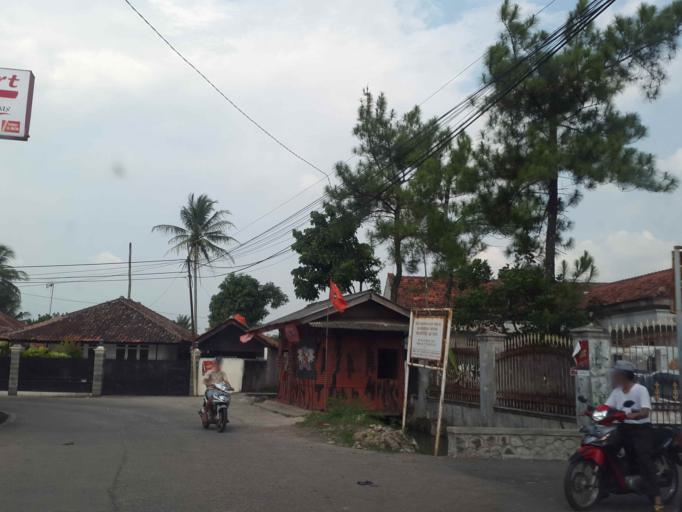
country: ID
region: West Java
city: Ciranjang-hilir
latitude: -6.7048
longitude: 107.1816
